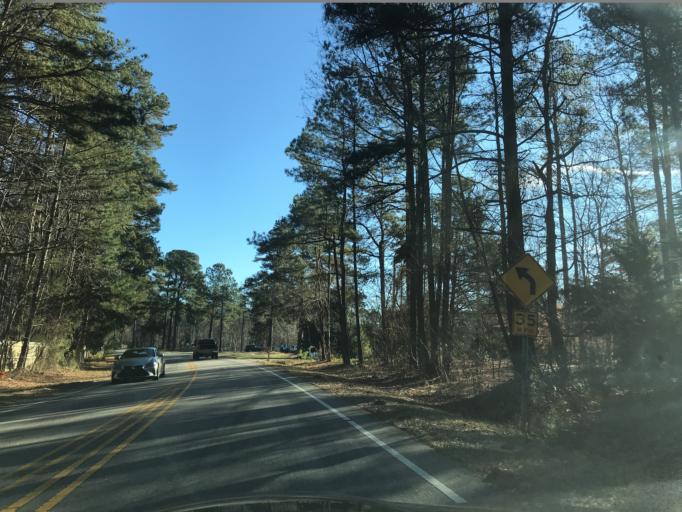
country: US
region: North Carolina
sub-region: Wake County
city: West Raleigh
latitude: 35.9077
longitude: -78.7130
